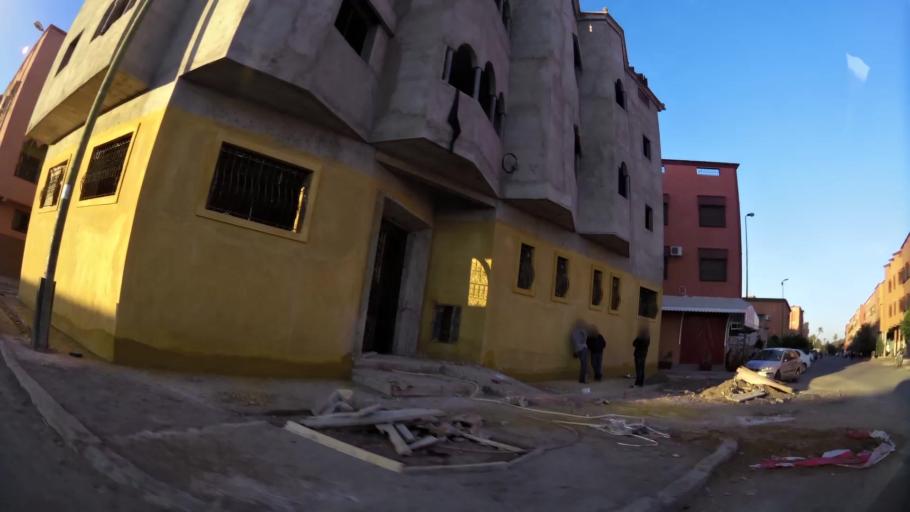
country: MA
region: Marrakech-Tensift-Al Haouz
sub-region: Marrakech
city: Marrakesh
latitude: 31.6356
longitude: -8.0370
